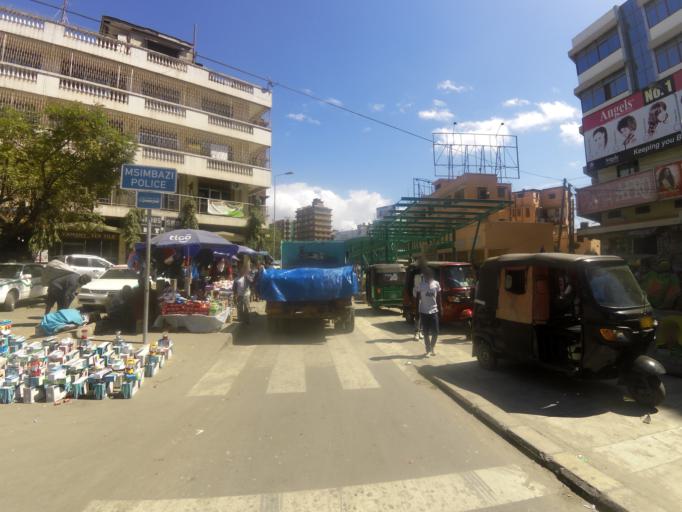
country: TZ
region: Dar es Salaam
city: Dar es Salaam
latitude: -6.8196
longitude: 39.2731
